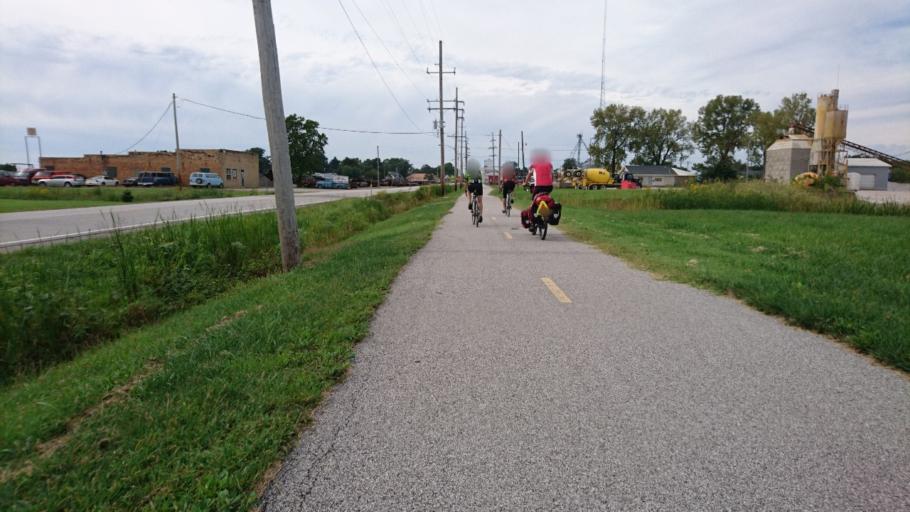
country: US
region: Illinois
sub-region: Madison County
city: Worden
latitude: 38.8928
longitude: -89.8408
